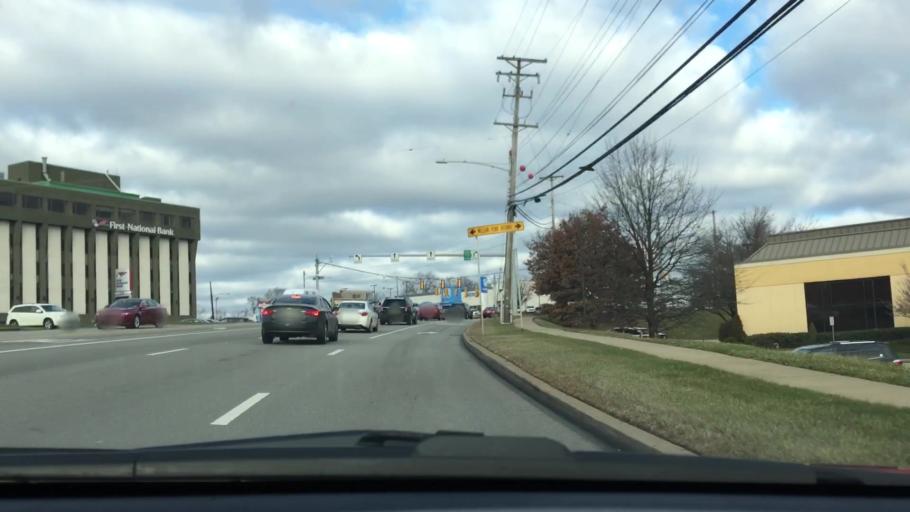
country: US
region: Pennsylvania
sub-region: Allegheny County
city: Monroeville
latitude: 40.4379
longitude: -79.7597
